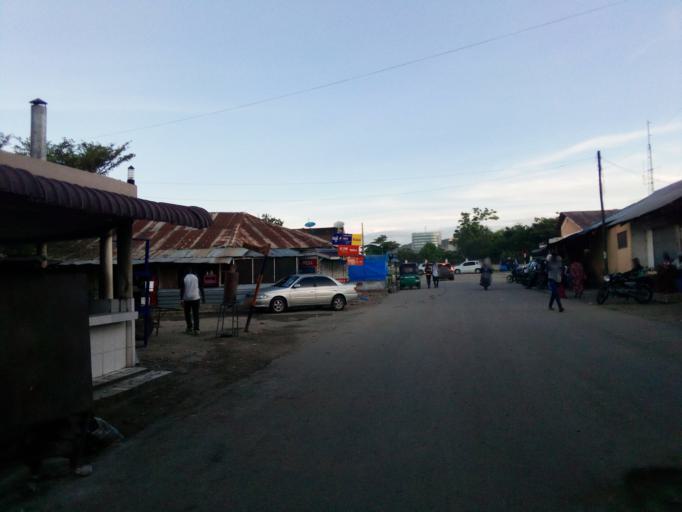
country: TZ
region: Dodoma
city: Dodoma
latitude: -6.1737
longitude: 35.7519
